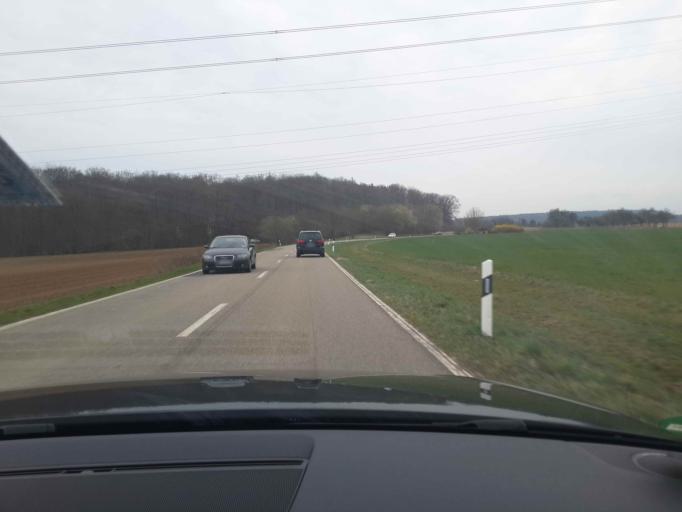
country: DE
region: Baden-Wuerttemberg
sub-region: Regierungsbezirk Stuttgart
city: Oedheim
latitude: 49.2311
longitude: 9.2689
